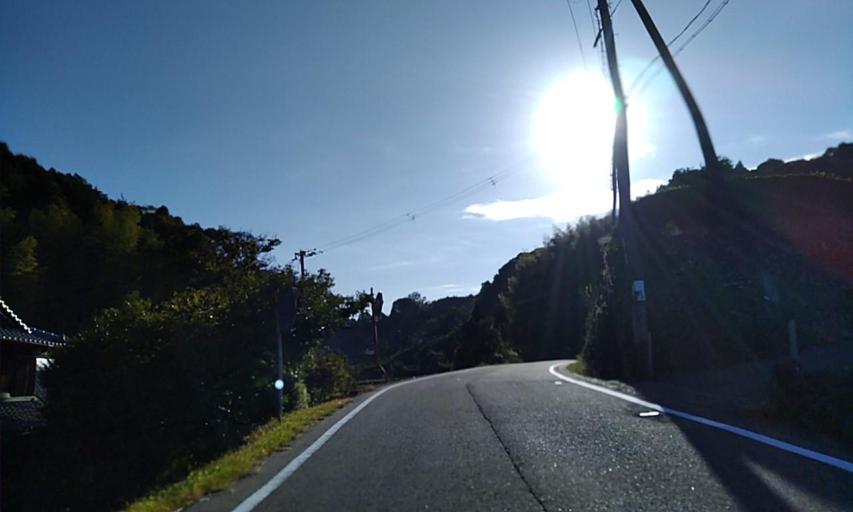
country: JP
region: Wakayama
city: Iwade
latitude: 34.1559
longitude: 135.2978
